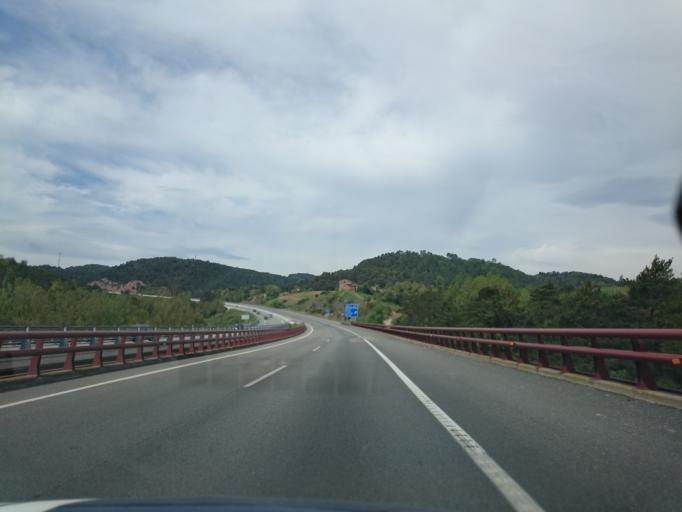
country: ES
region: Catalonia
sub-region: Provincia de Barcelona
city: Muntanyola
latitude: 41.9329
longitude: 2.1594
